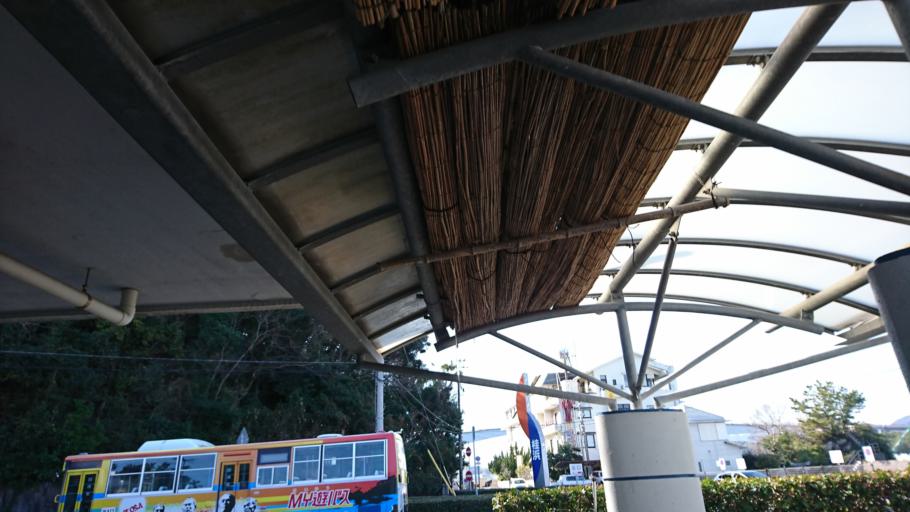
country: JP
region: Kochi
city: Kochi-shi
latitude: 33.4994
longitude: 133.5739
